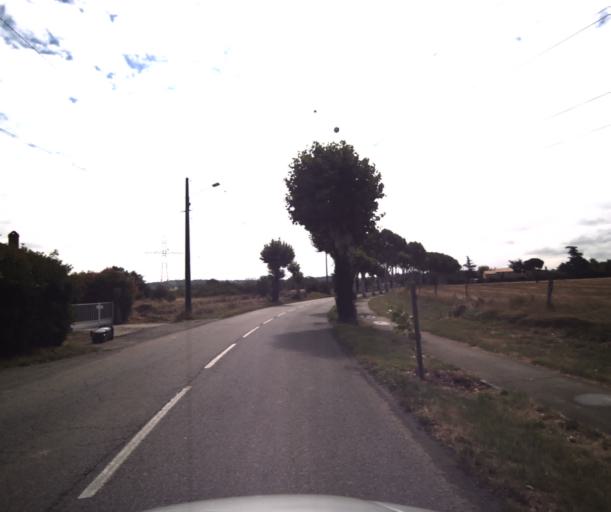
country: FR
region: Midi-Pyrenees
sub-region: Departement de la Haute-Garonne
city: Portet-sur-Garonne
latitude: 43.5303
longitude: 1.3948
